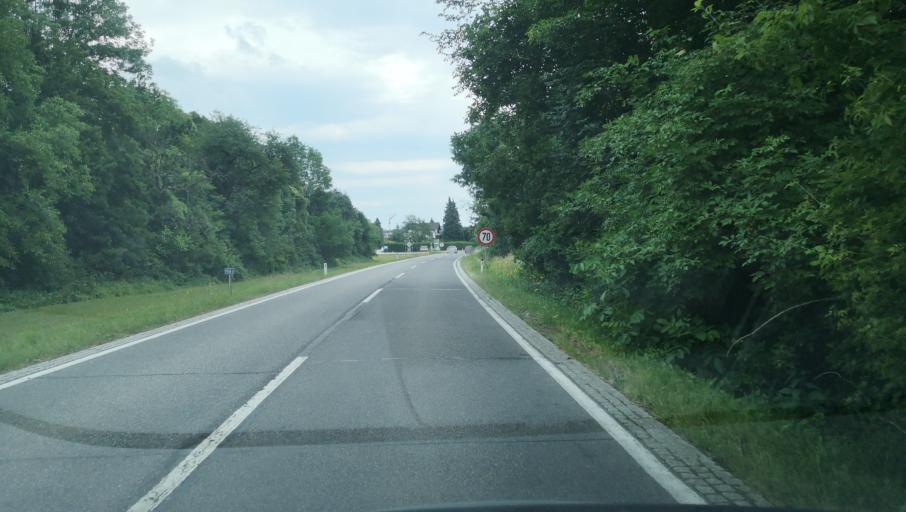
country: AT
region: Lower Austria
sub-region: Politischer Bezirk Melk
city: Klein-Poechlarn
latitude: 48.2183
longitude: 15.2059
